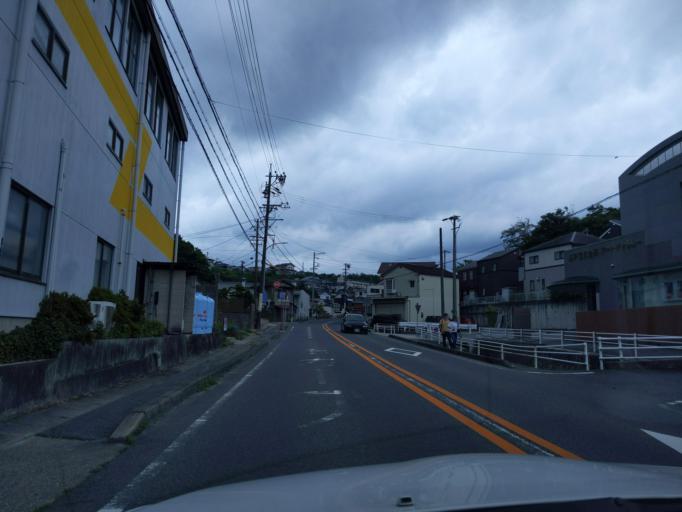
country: JP
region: Aichi
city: Seto
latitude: 35.2222
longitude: 137.1016
